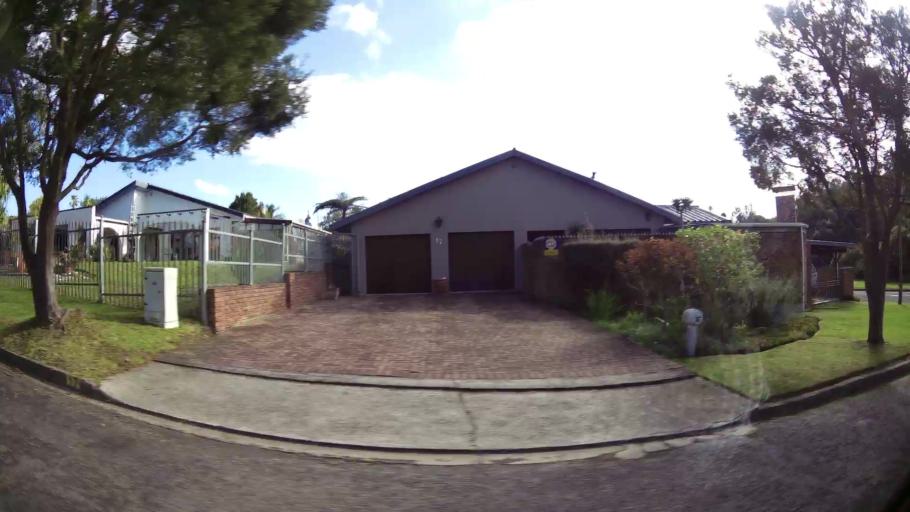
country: ZA
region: Western Cape
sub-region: Eden District Municipality
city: George
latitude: -33.9541
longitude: 22.4776
